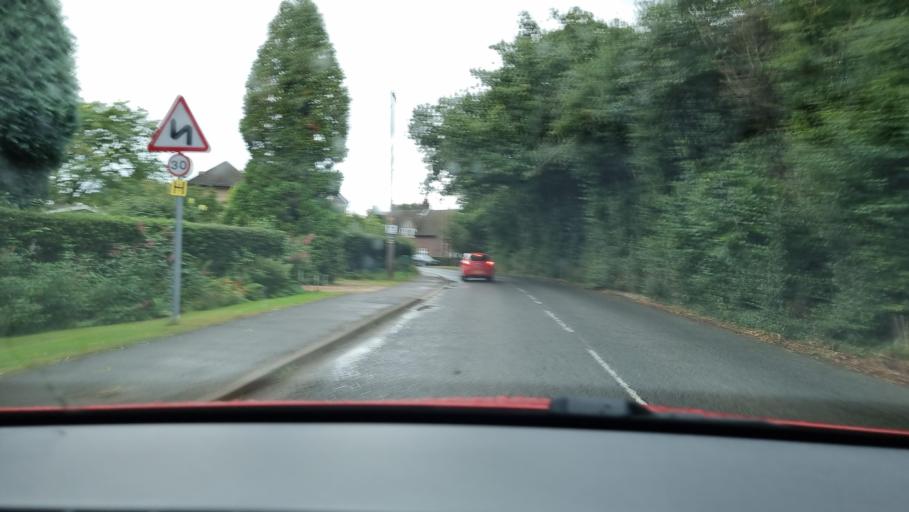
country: GB
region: England
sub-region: Hertfordshire
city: Berkhamsted
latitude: 51.7345
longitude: -0.5848
